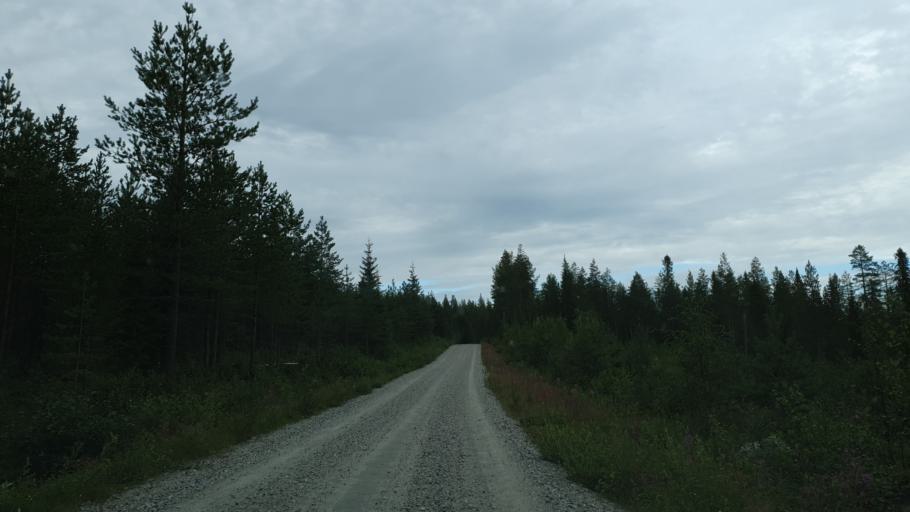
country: FI
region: Kainuu
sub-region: Kehys-Kainuu
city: Kuhmo
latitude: 64.4504
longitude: 29.5620
